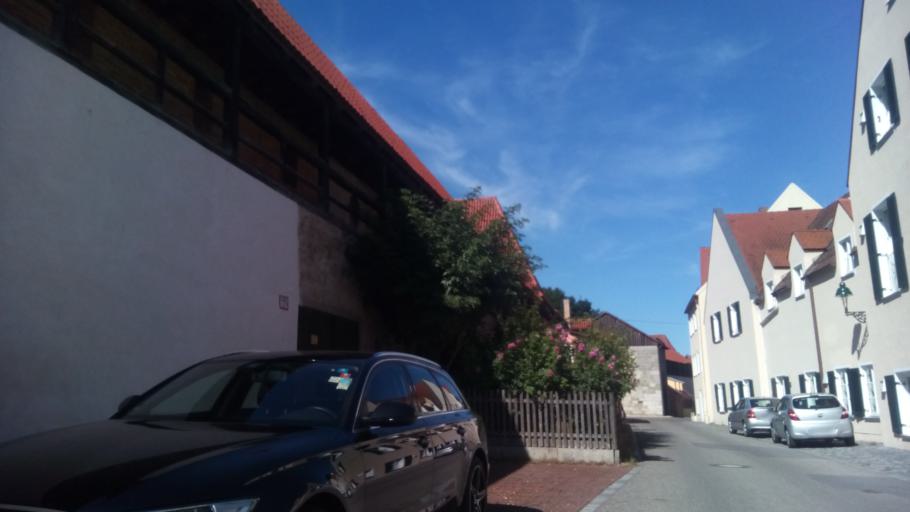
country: DE
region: Bavaria
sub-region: Swabia
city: Noerdlingen
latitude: 48.8530
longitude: 10.4847
